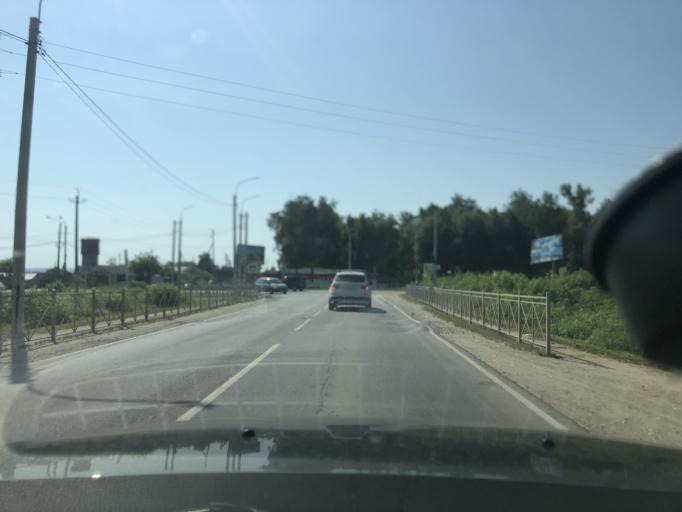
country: RU
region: Tula
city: Dubna
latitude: 54.1051
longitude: 37.1097
